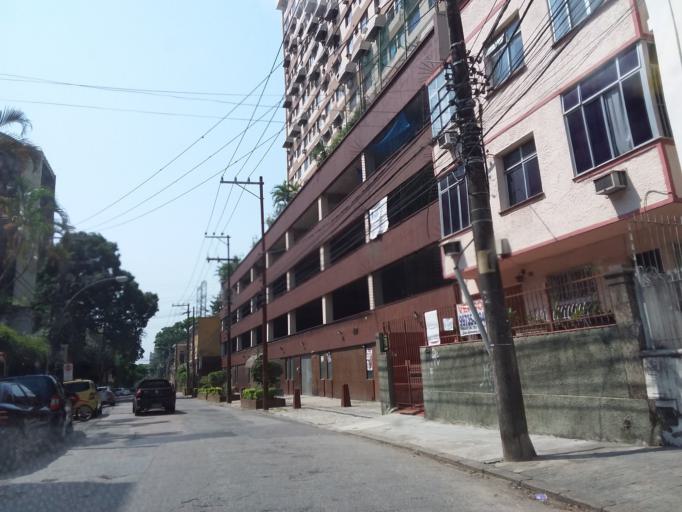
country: BR
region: Rio de Janeiro
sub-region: Rio De Janeiro
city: Rio de Janeiro
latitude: -22.9288
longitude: -43.2081
